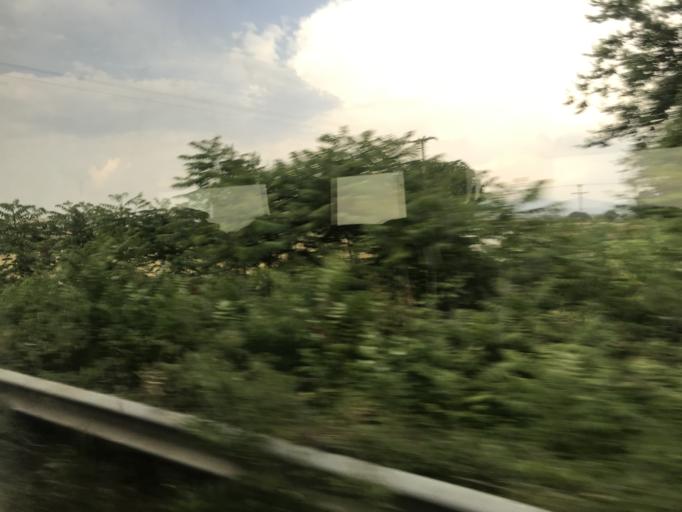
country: GR
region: East Macedonia and Thrace
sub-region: Nomos Rodopis
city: Sapes
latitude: 40.9704
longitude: 25.6438
